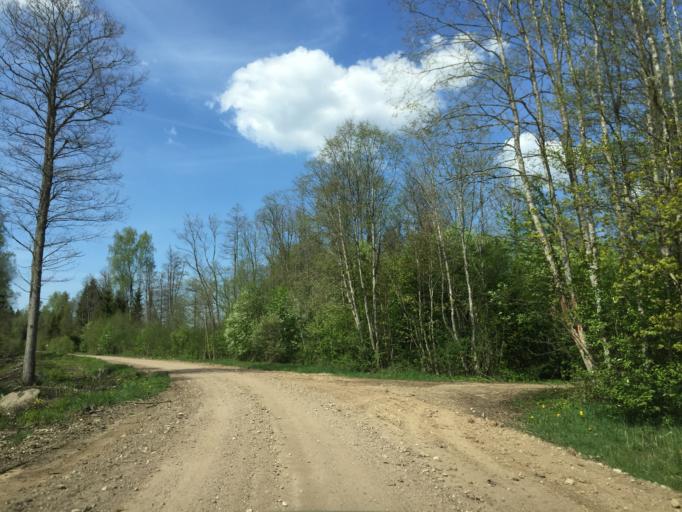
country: LV
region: Limbazu Rajons
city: Limbazi
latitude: 57.3873
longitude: 24.6020
